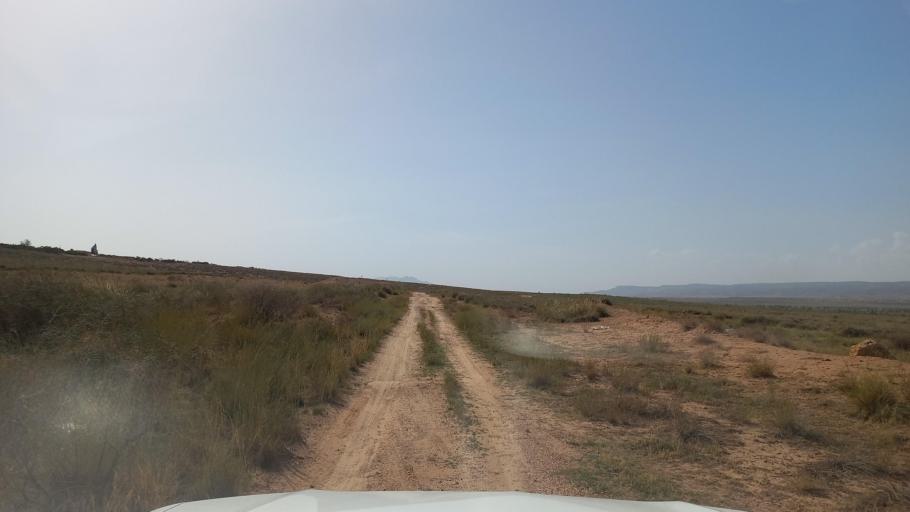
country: TN
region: Al Qasrayn
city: Kasserine
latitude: 35.2145
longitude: 8.9925
